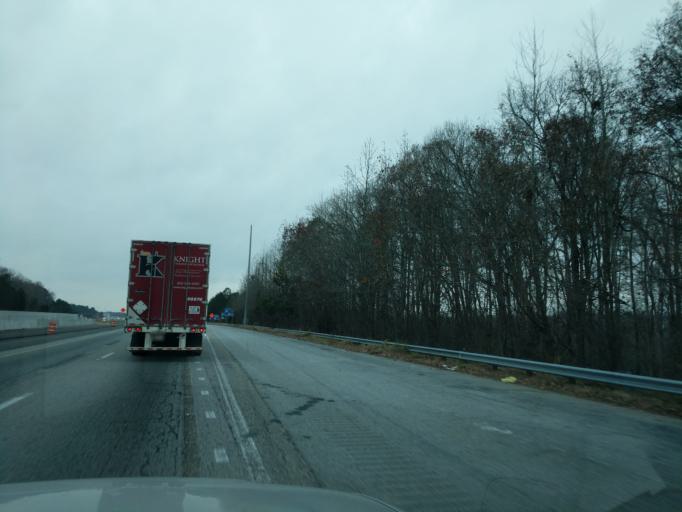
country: US
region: Georgia
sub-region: Gwinnett County
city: Buford
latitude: 34.0576
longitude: -83.9817
